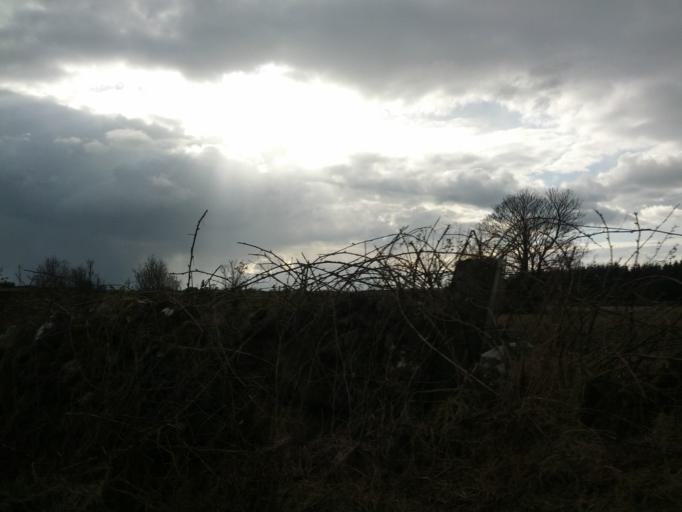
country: IE
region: Connaught
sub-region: County Galway
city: Athenry
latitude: 53.4302
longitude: -8.6228
